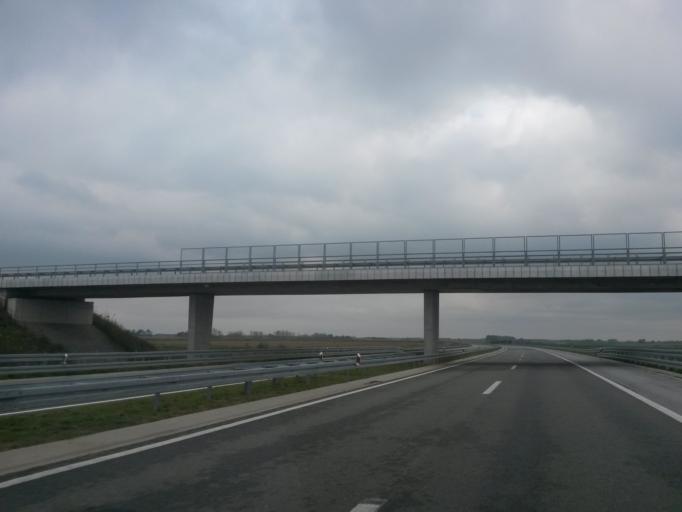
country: HR
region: Osjecko-Baranjska
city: Gorjani
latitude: 45.3498
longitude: 18.4011
